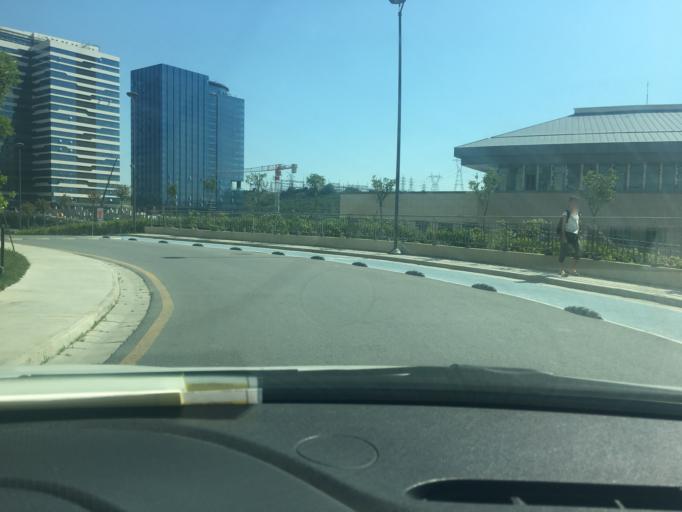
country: TR
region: Istanbul
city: Sisli
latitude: 41.0896
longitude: 28.9499
